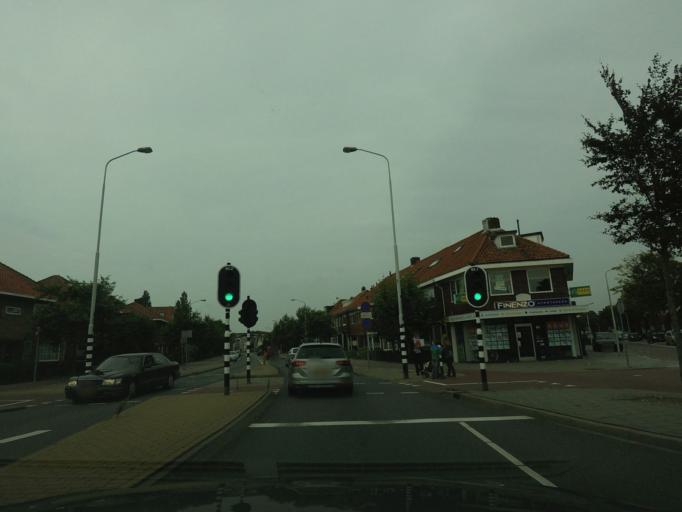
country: NL
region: North Holland
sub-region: Gemeente Zaanstad
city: Zaanstad
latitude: 52.4851
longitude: 4.8060
